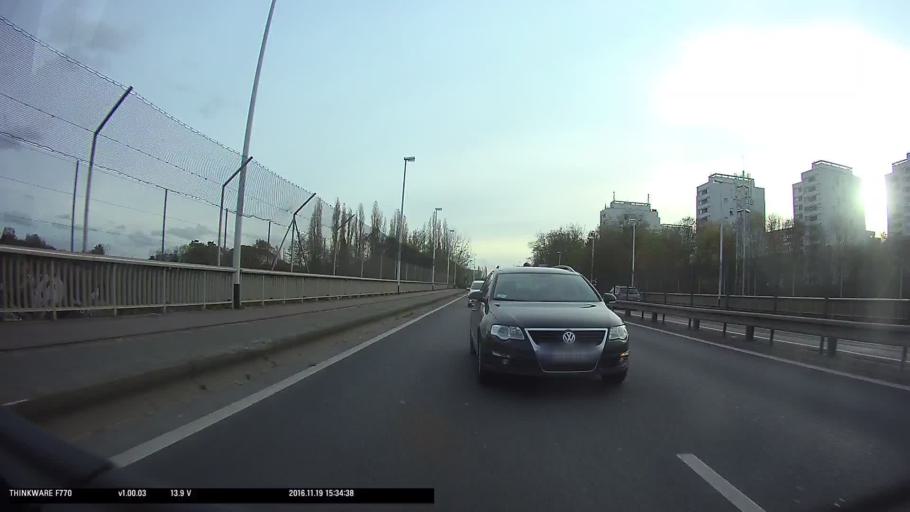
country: FR
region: Ile-de-France
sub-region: Departement du Val-d'Oise
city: Cergy-Pontoise
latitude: 49.0529
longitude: 2.0815
